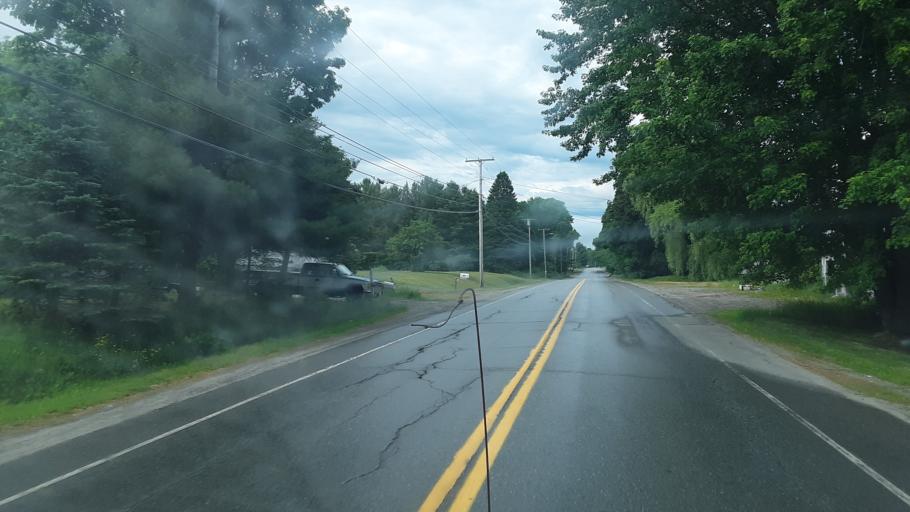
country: US
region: Maine
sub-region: Penobscot County
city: Lincoln
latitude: 45.3829
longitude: -68.4984
